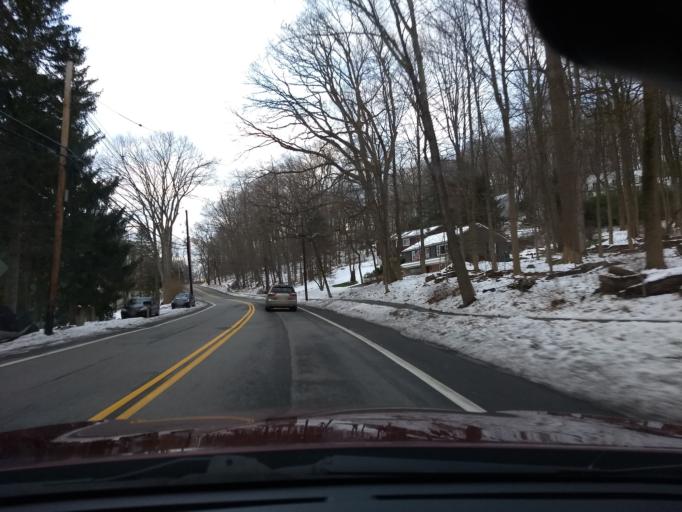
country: US
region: New Jersey
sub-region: Morris County
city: Morristown
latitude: 40.8080
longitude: -74.4951
